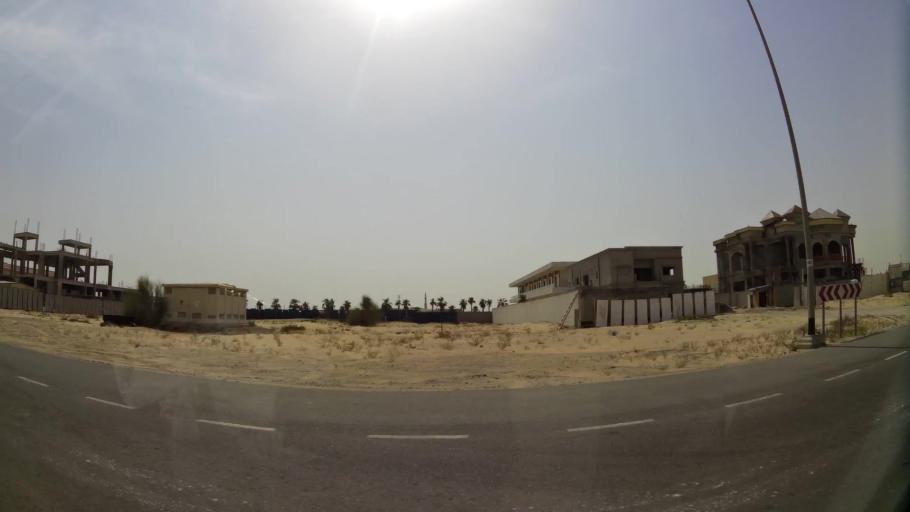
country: AE
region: Ash Shariqah
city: Sharjah
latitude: 25.2469
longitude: 55.4789
